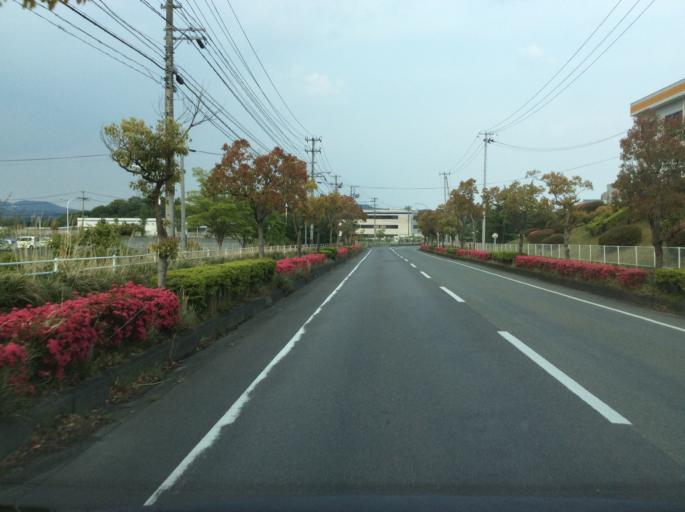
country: JP
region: Fukushima
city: Iwaki
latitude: 37.0782
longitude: 140.8477
